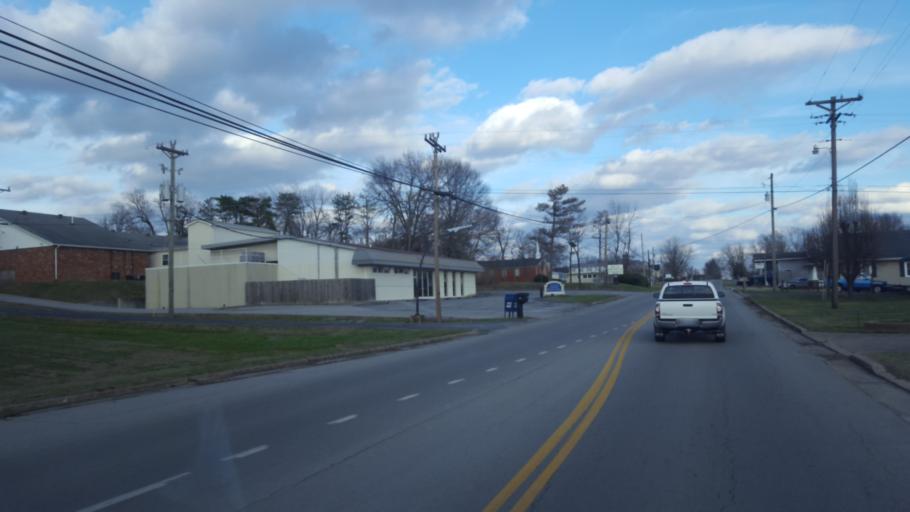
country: US
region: Kentucky
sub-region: Fleming County
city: Flemingsburg
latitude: 38.4200
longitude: -83.7487
